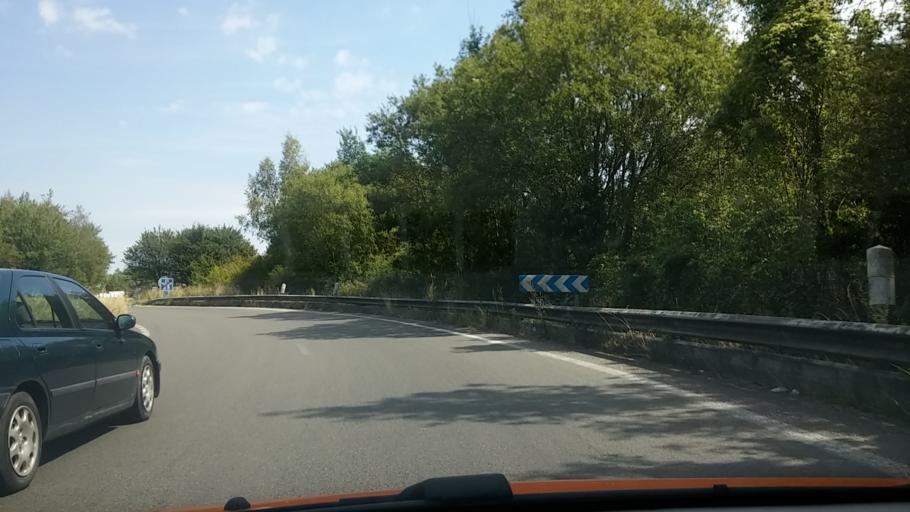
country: FR
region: Ile-de-France
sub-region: Departement de Seine-et-Marne
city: Serris
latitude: 48.8312
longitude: 2.7968
